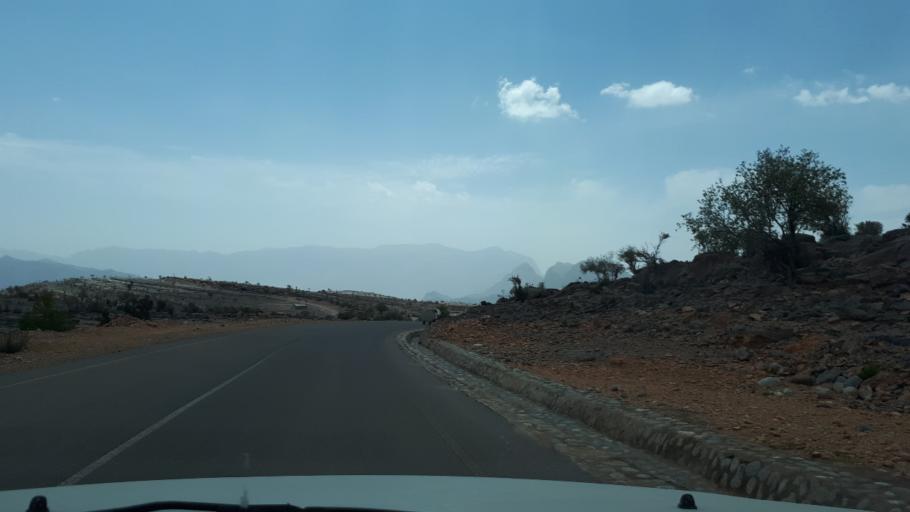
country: OM
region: Muhafazat ad Dakhiliyah
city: Bahla'
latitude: 23.2095
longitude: 57.2023
